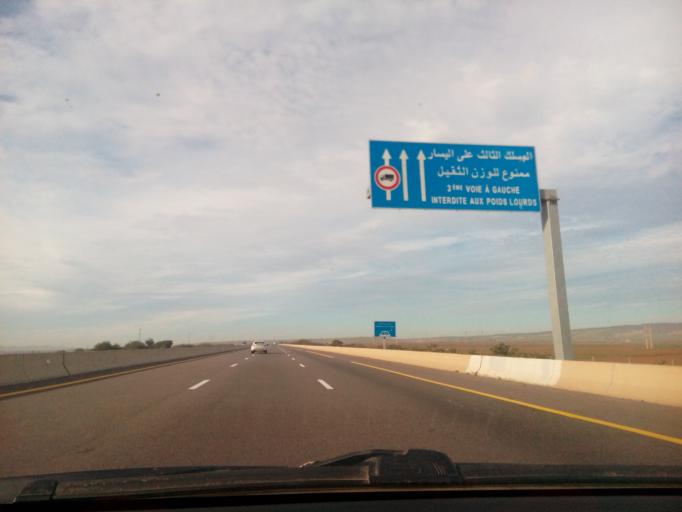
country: DZ
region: Mascara
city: Sig
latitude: 35.5758
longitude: -0.2682
